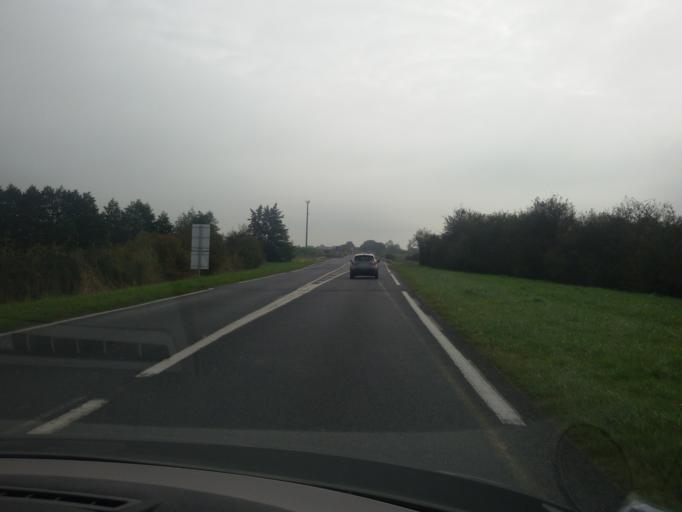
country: FR
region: Lower Normandy
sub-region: Departement du Calvados
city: Dozule
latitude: 49.2326
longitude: -0.0890
